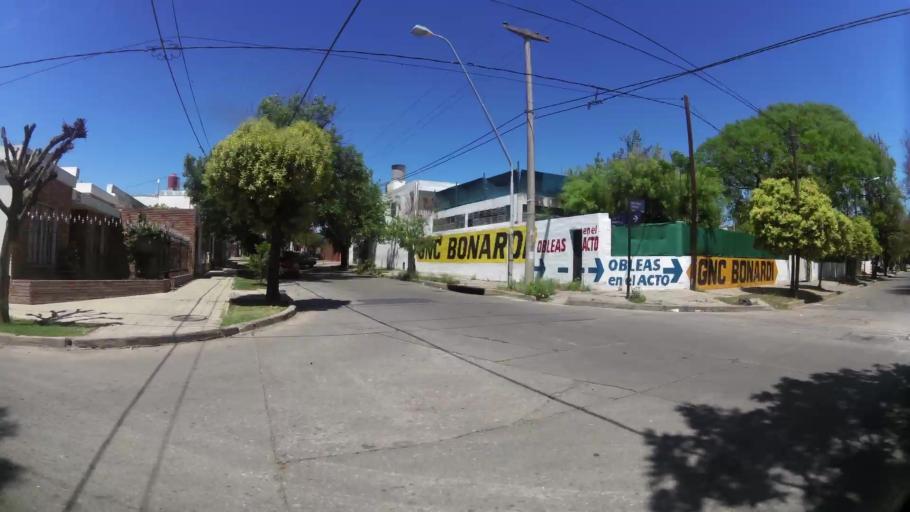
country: AR
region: Cordoba
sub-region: Departamento de Capital
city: Cordoba
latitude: -31.4149
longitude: -64.2154
